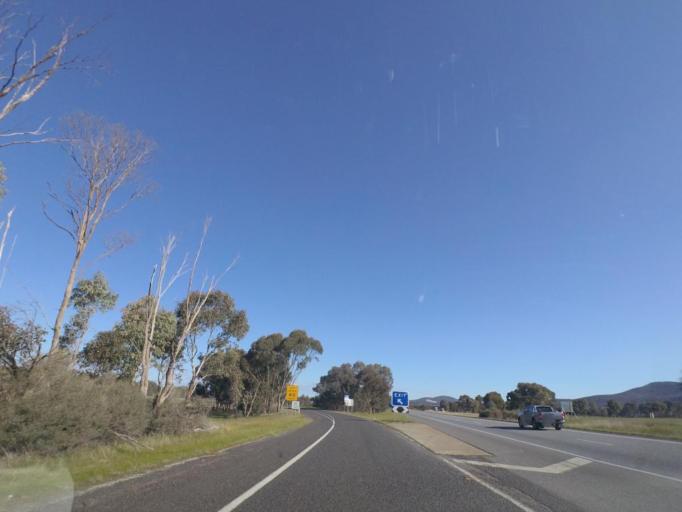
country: AU
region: Victoria
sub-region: Wangaratta
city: Wangaratta
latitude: -36.4218
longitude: 146.2639
